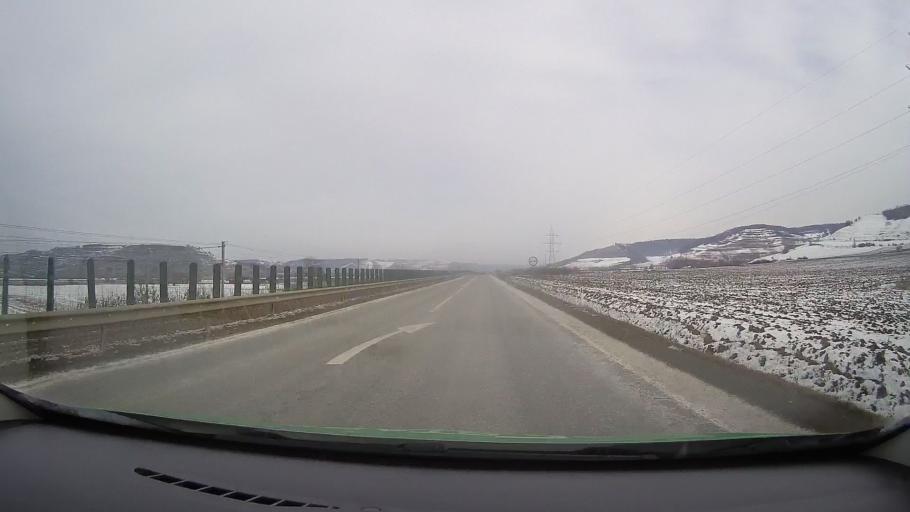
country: RO
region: Sibiu
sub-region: Comuna Alma
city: Alma
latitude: 46.1880
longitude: 24.4535
